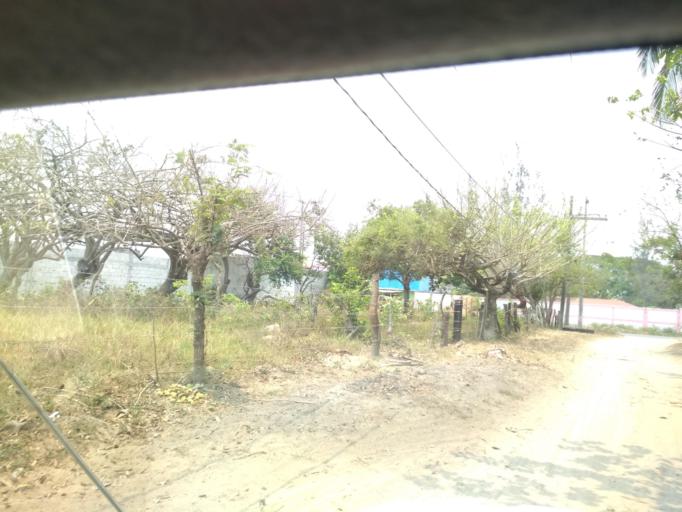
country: MX
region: Veracruz
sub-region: Veracruz
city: Delfino Victoria (Santa Fe)
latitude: 19.2108
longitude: -96.2679
